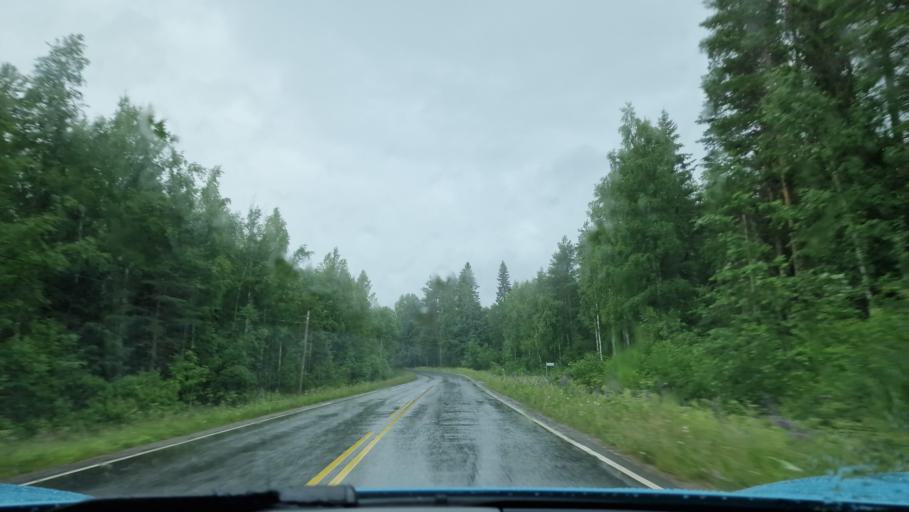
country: FI
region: Southern Ostrobothnia
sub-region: Jaerviseutu
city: Soini
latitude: 62.8269
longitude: 24.3417
